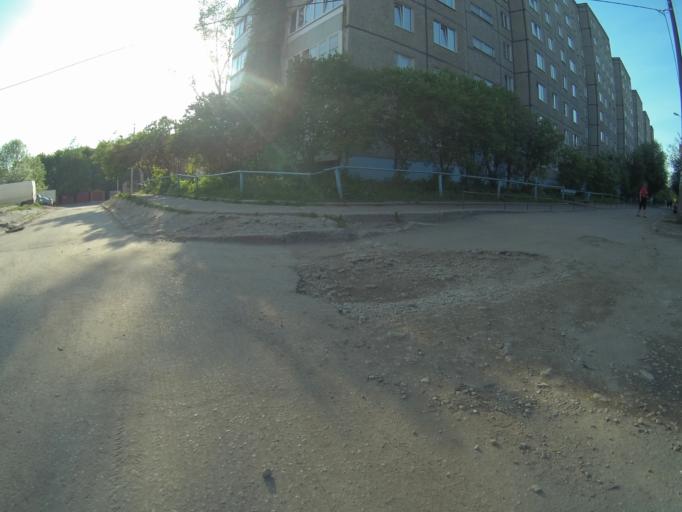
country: RU
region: Vladimir
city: Kommunar
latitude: 56.1671
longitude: 40.4566
